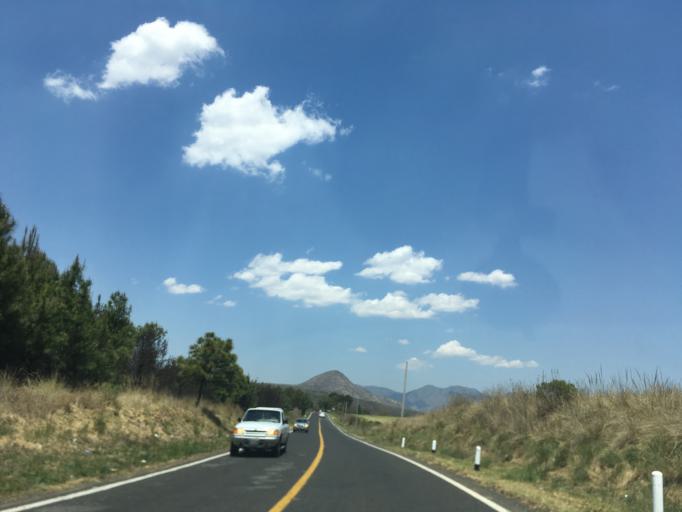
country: MX
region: Mexico
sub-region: Chalco
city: Zopoco
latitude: 19.7903
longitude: -102.0237
